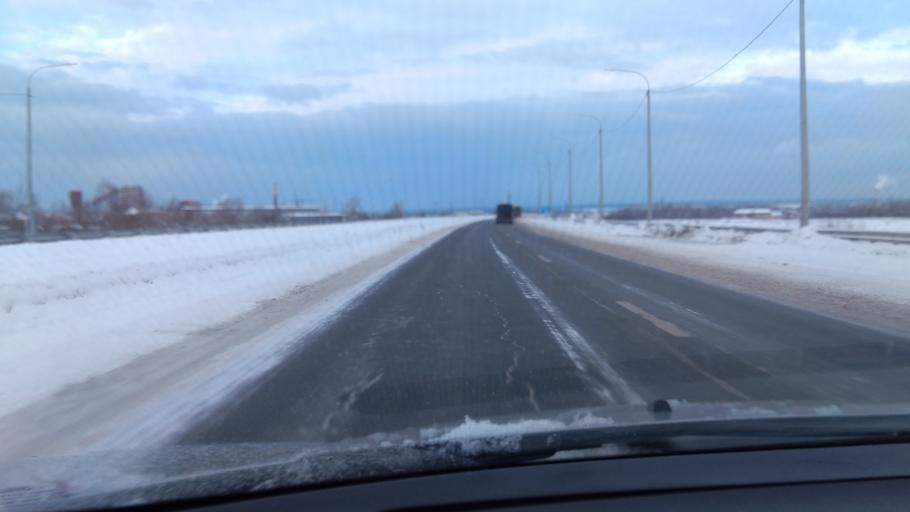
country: RU
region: Sverdlovsk
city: Tsementnyy
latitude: 57.4692
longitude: 60.1831
